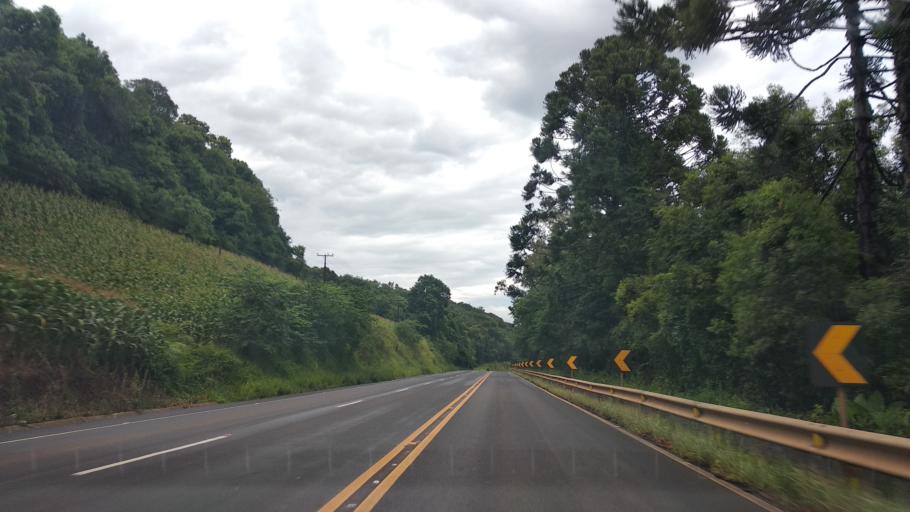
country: BR
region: Santa Catarina
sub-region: Videira
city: Videira
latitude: -27.0867
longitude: -51.2411
